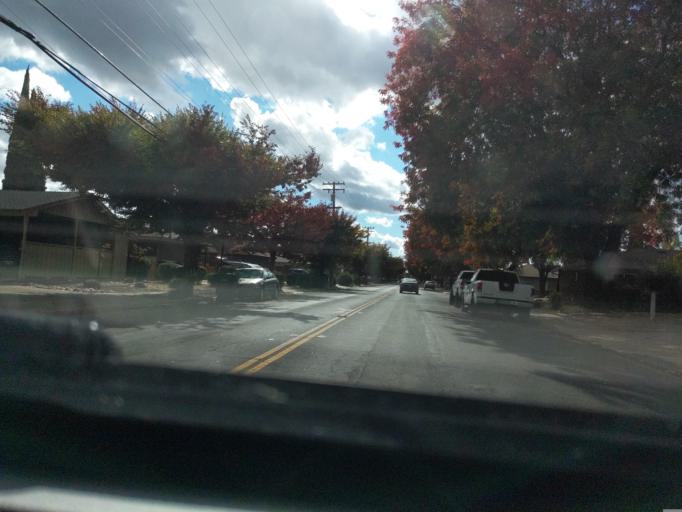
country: US
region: California
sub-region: Stanislaus County
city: Modesto
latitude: 37.6717
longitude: -120.9668
